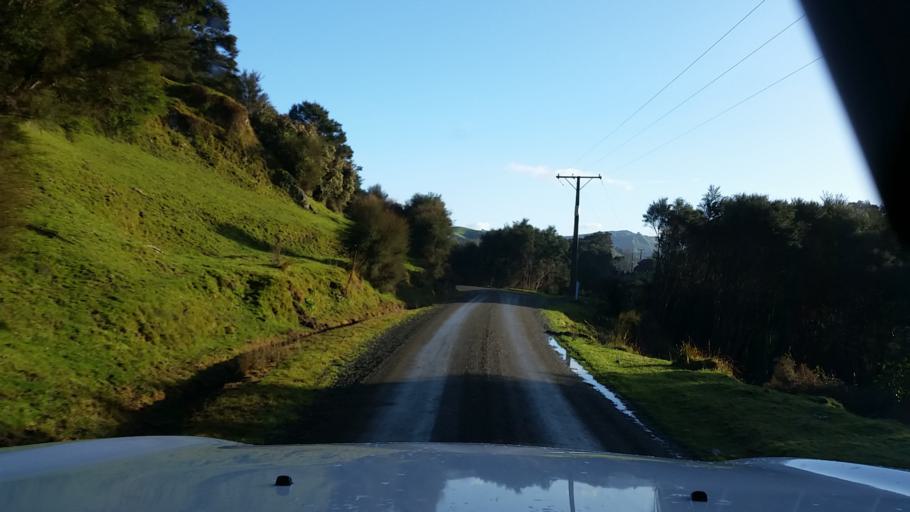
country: NZ
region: Wellington
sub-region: South Wairarapa District
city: Waipawa
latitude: -41.3259
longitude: 175.6599
